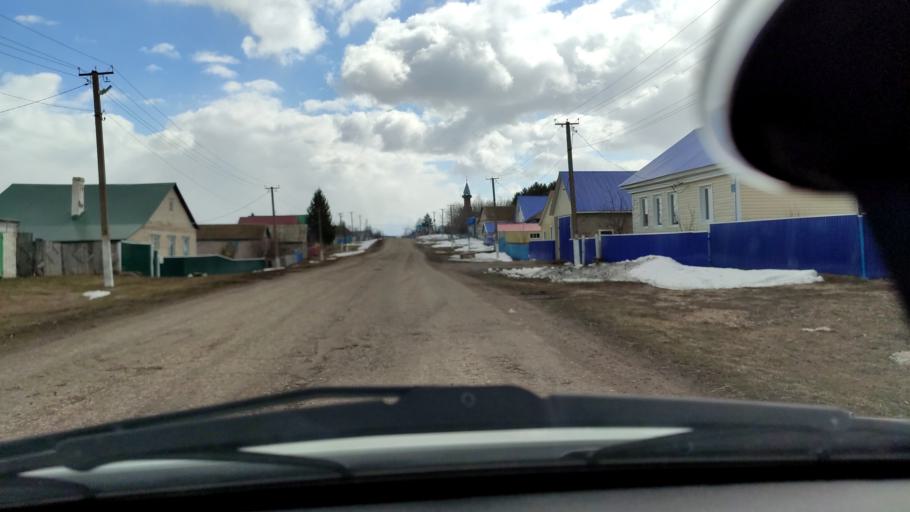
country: RU
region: Bashkortostan
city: Tolbazy
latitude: 54.1712
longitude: 55.9564
